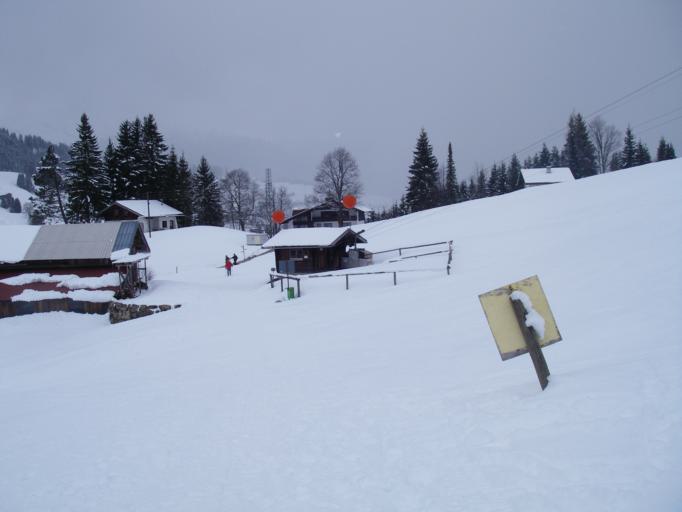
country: AT
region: Vorarlberg
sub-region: Politischer Bezirk Bregenz
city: Mittelberg
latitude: 47.3289
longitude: 10.1714
